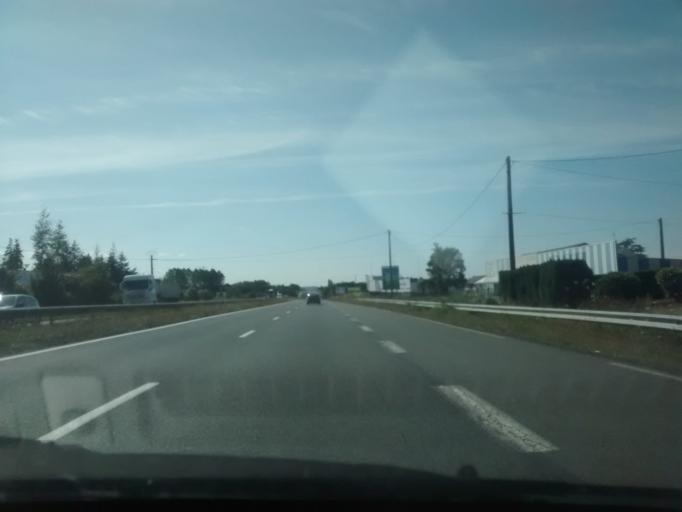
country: FR
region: Brittany
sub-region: Departement des Cotes-d'Armor
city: Saint-Agathon
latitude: 48.5451
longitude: -3.0890
